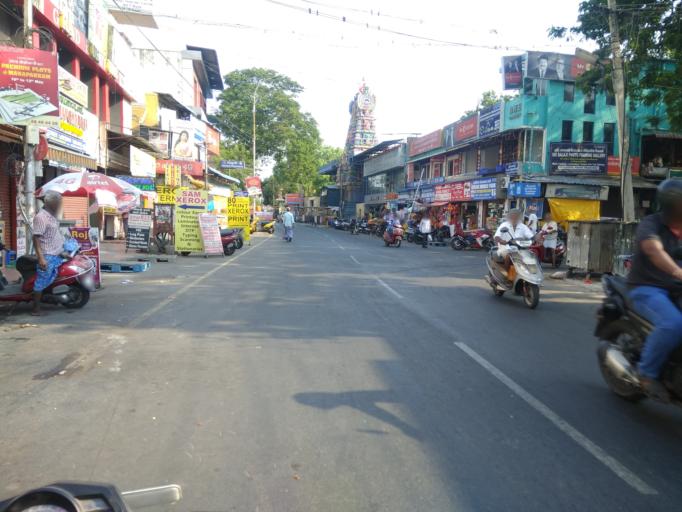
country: IN
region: Tamil Nadu
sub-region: Kancheepuram
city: Saint Thomas Mount
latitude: 12.9856
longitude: 80.1884
